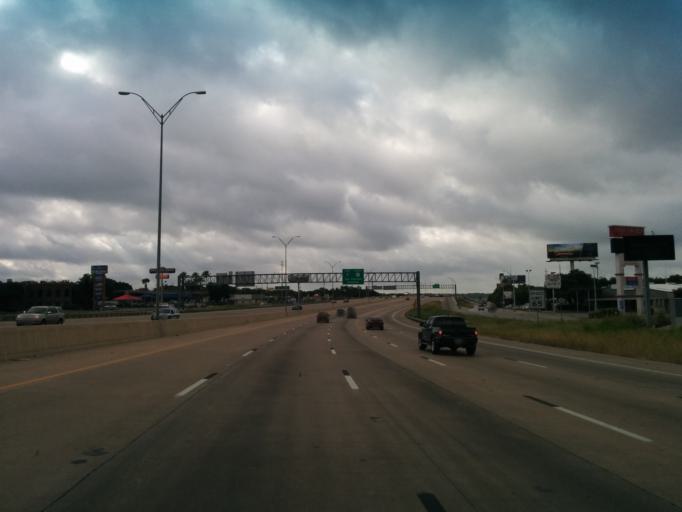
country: US
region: Texas
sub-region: Bexar County
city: Balcones Heights
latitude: 29.4841
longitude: -98.5303
